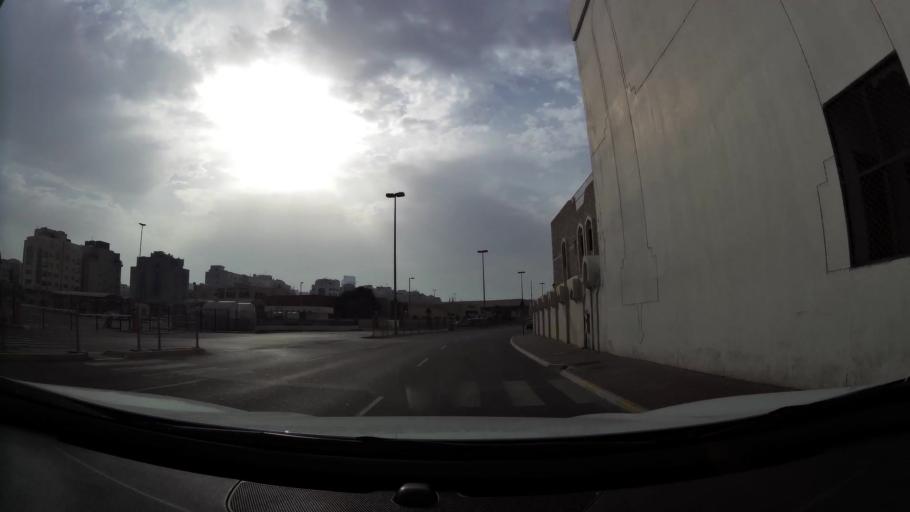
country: AE
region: Abu Dhabi
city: Abu Dhabi
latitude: 24.4693
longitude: 54.3769
